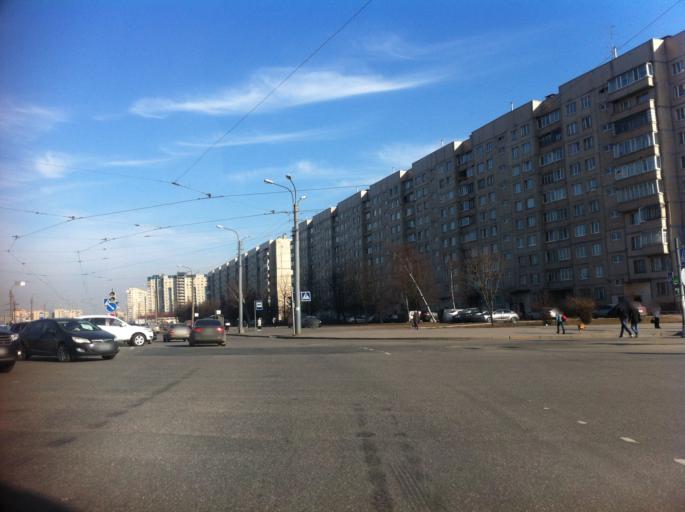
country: RU
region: St.-Petersburg
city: Uritsk
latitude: 59.8601
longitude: 30.2057
